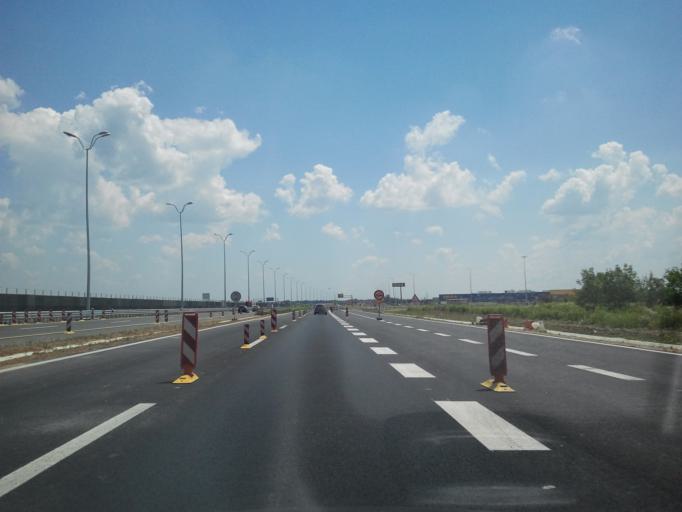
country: HR
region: Grad Zagreb
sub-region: Sesvete
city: Sesvete
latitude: 45.7969
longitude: 16.1463
